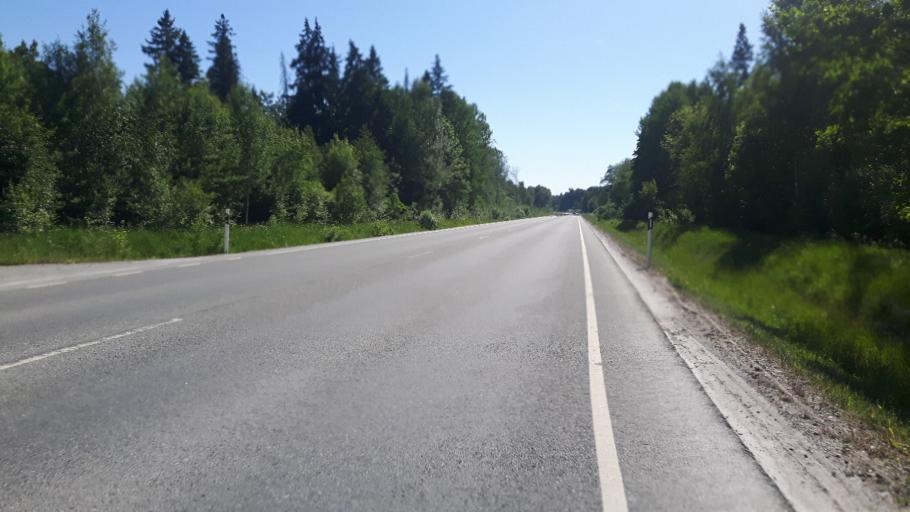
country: EE
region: Raplamaa
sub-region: Rapla vald
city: Rapla
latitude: 59.0293
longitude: 24.8203
